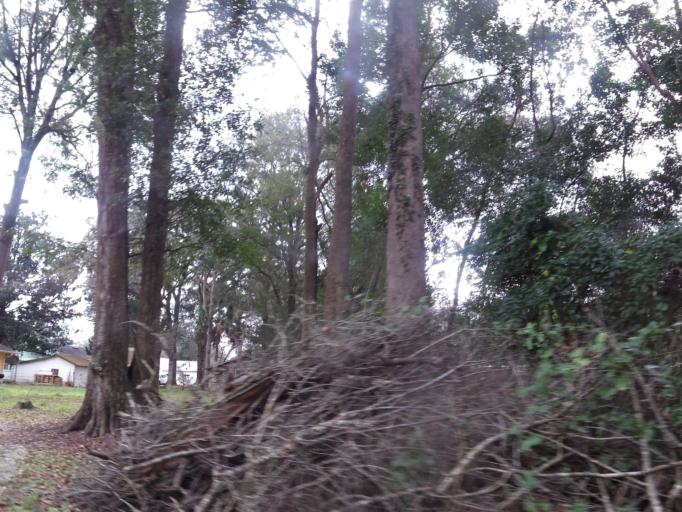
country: US
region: Florida
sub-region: Alachua County
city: High Springs
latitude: 29.8225
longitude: -82.6025
